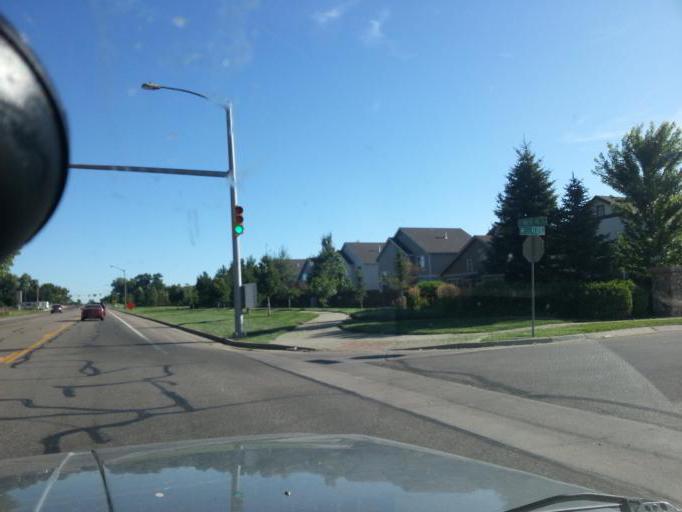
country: US
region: Colorado
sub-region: Larimer County
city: Fort Collins
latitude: 40.4971
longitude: -105.0392
